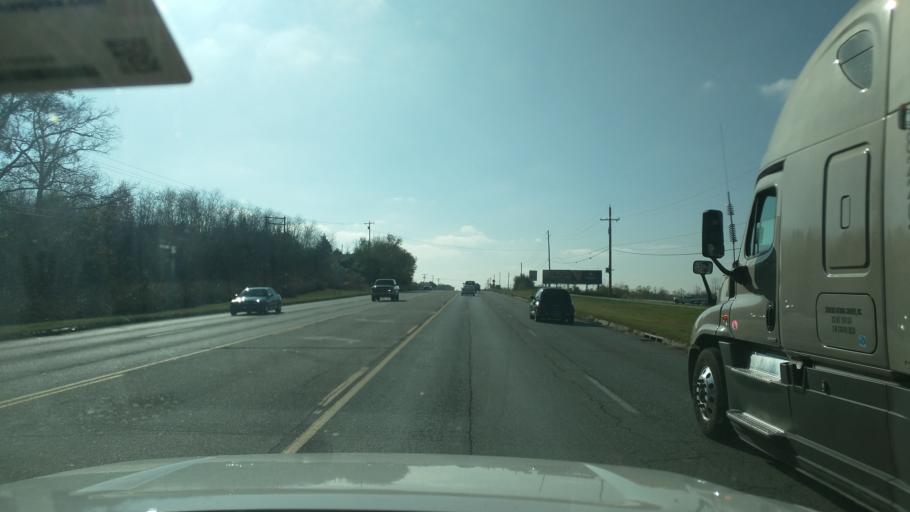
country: US
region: Oklahoma
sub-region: Washington County
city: Bartlesville
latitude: 36.7046
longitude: -95.9352
